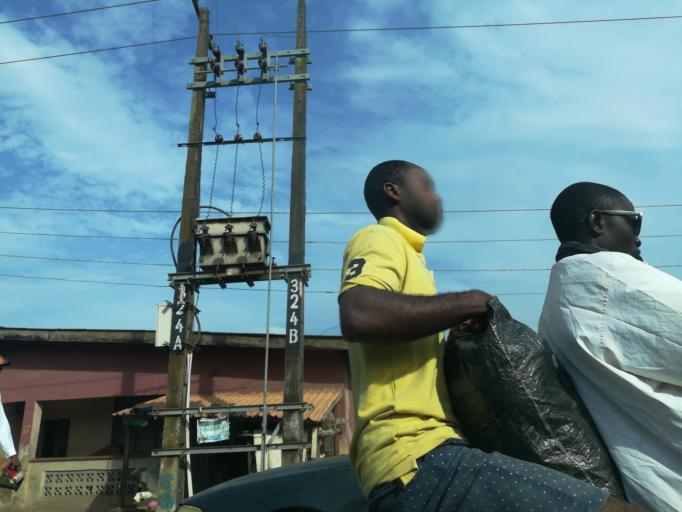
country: NG
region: Lagos
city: Ojota
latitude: 6.6056
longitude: 3.4214
